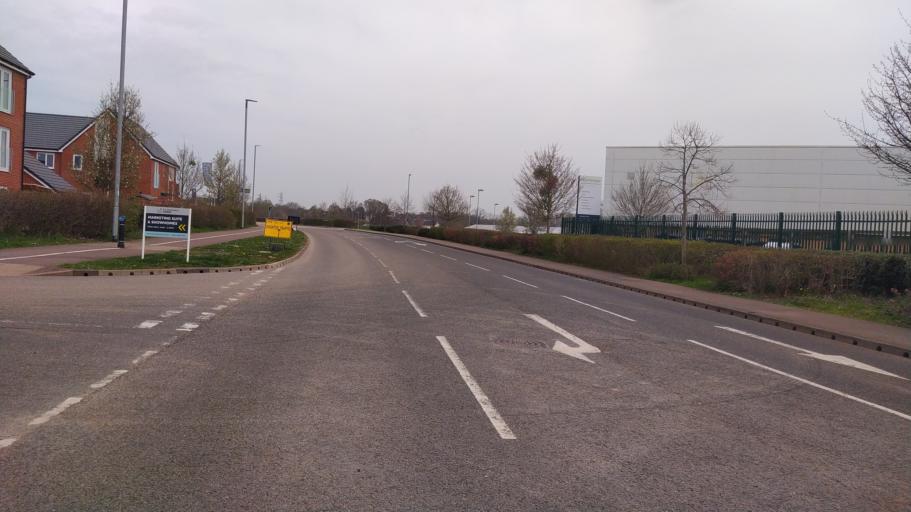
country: GB
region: England
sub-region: Somerset
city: Taunton
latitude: 51.0257
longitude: -3.1389
